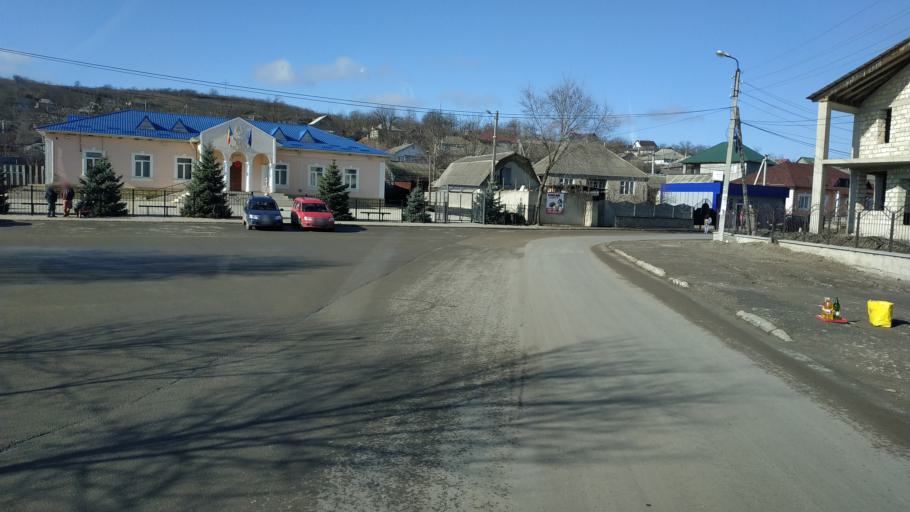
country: MD
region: Hincesti
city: Hincesti
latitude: 46.9298
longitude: 28.6507
